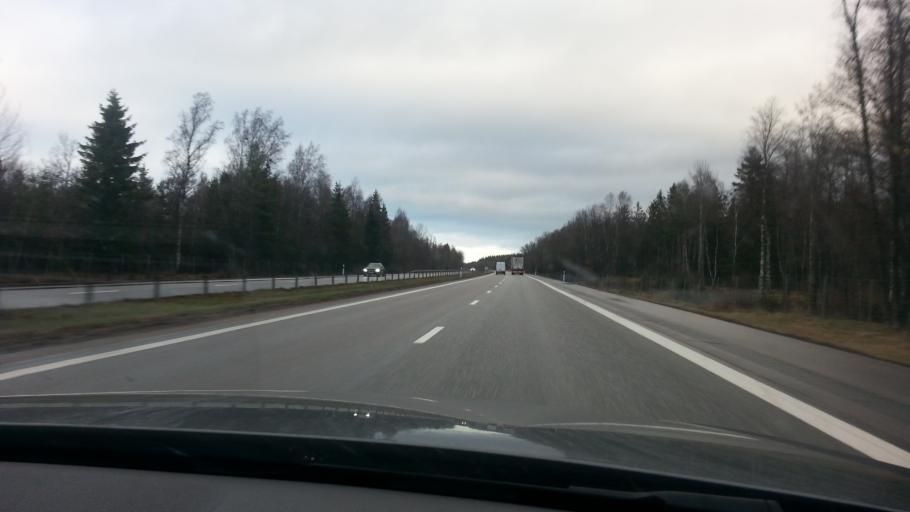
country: SE
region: Joenkoeping
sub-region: Jonkopings Kommun
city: Asa
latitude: 58.0905
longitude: 14.5484
